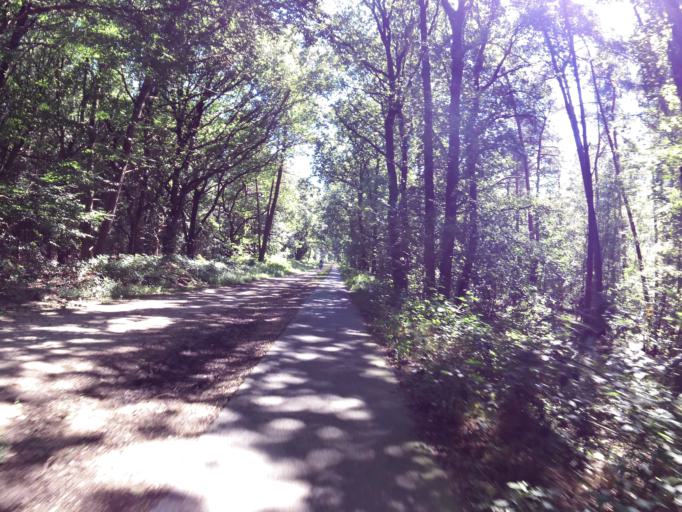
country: NL
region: Gelderland
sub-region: Gemeente Groesbeek
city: Berg en Dal
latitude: 51.8007
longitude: 5.8819
